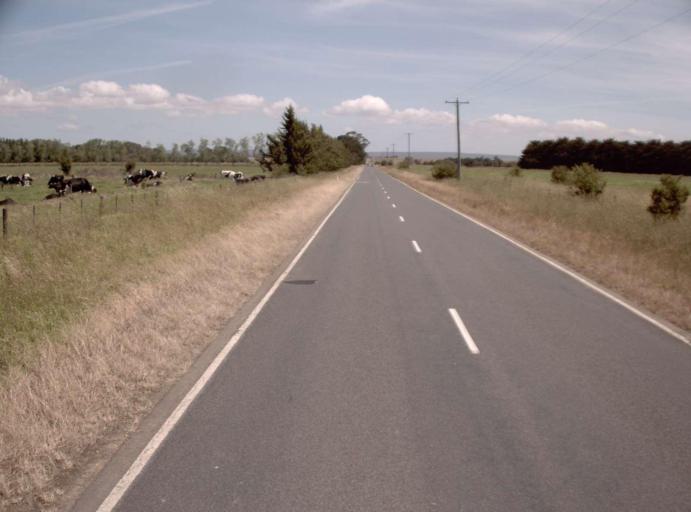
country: AU
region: Victoria
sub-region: Wellington
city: Heyfield
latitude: -38.0896
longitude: 146.8667
